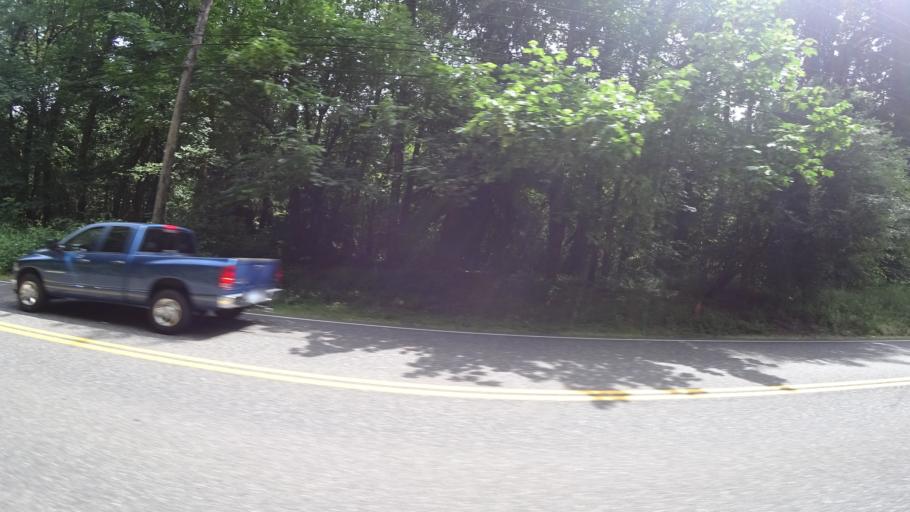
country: US
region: Oregon
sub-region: Clackamas County
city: Milwaukie
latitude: 45.4653
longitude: -122.6756
